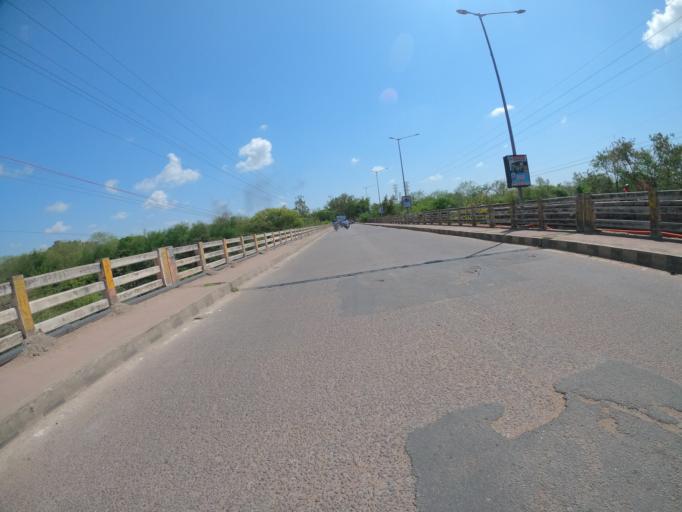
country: IN
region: Telangana
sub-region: Hyderabad
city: Hyderabad
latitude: 17.3716
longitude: 78.4047
